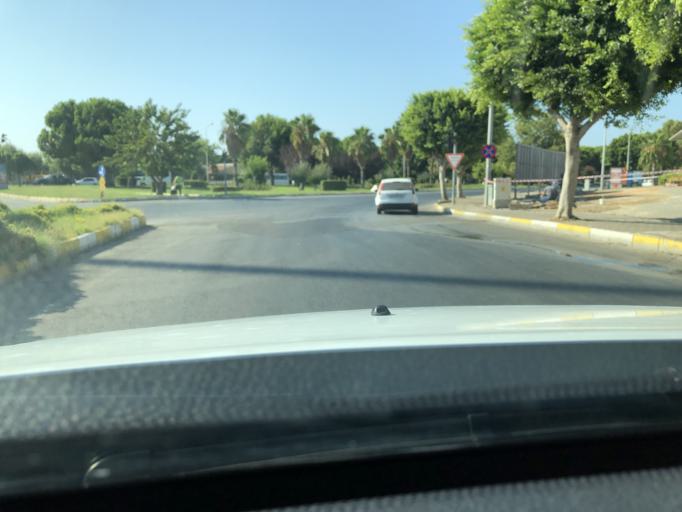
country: TR
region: Antalya
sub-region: Manavgat
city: Side
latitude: 36.7767
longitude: 31.3970
